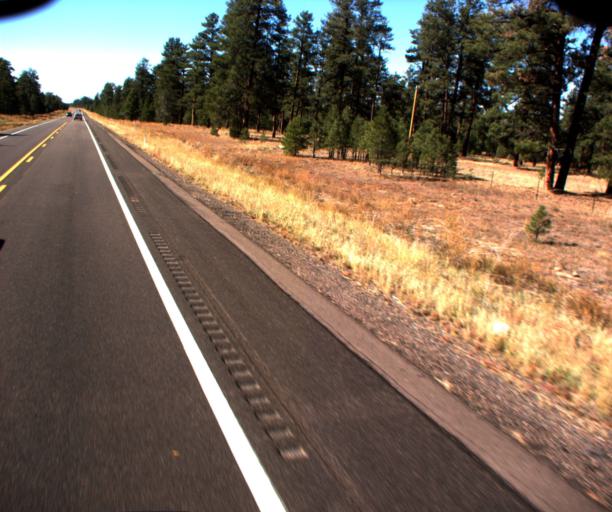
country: US
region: Arizona
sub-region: Apache County
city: Saint Michaels
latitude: 35.6943
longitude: -109.2685
